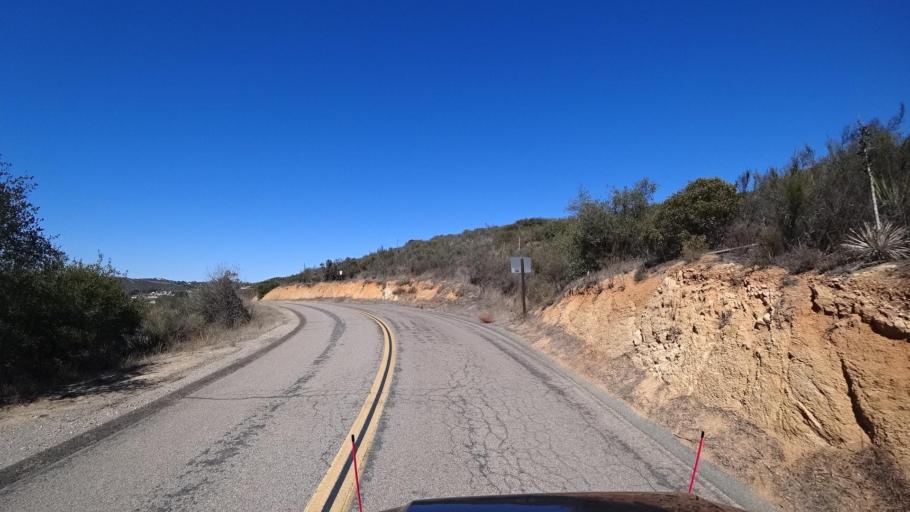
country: US
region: California
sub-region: San Diego County
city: Alpine
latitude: 32.7991
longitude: -116.7699
